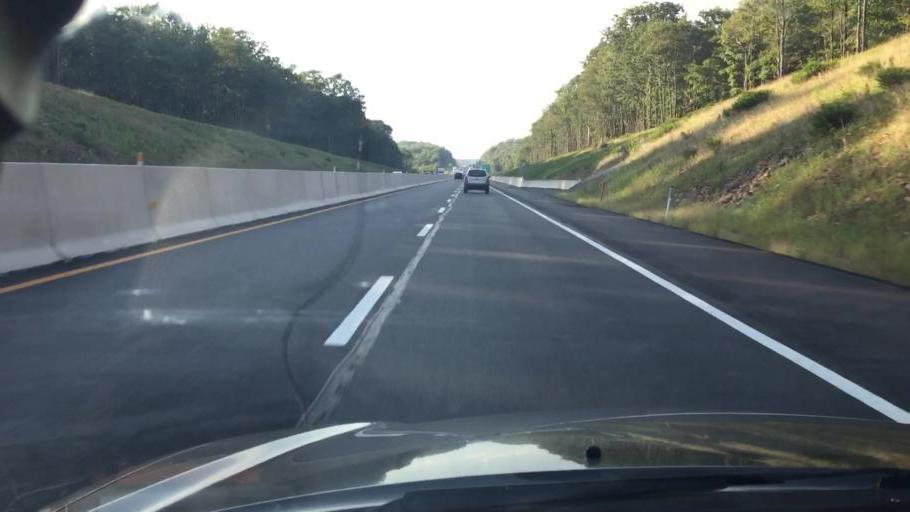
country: US
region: Pennsylvania
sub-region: Luzerne County
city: White Haven
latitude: 41.0507
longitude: -75.6751
